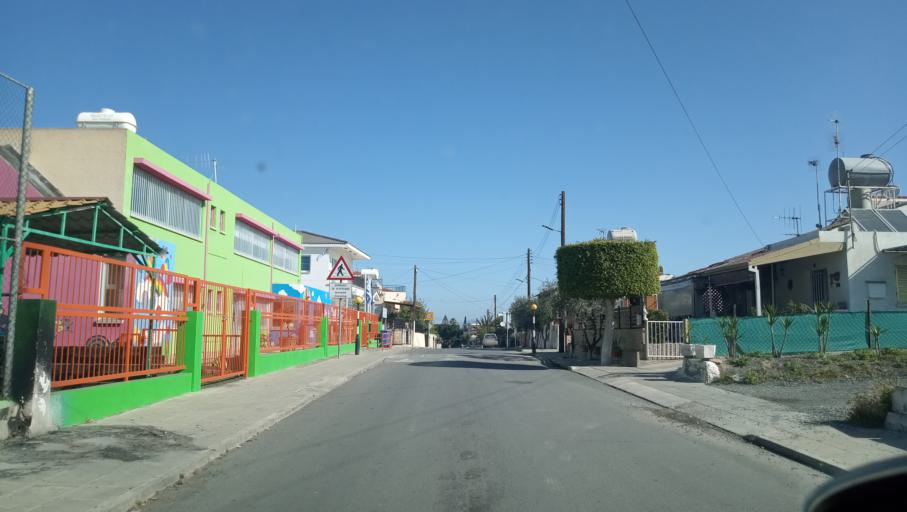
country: CY
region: Lefkosia
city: Tseri
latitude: 35.0734
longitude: 33.3314
